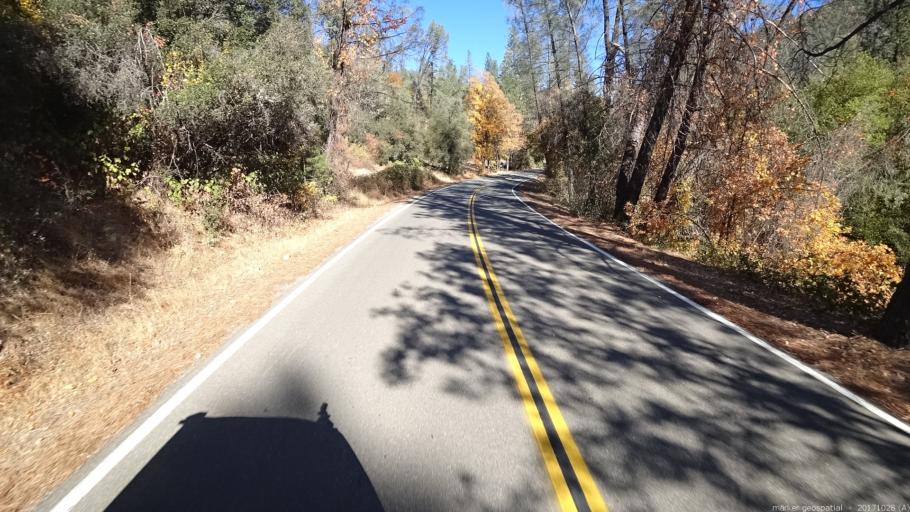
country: US
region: California
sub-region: Trinity County
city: Lewiston
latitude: 40.7333
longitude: -122.6271
